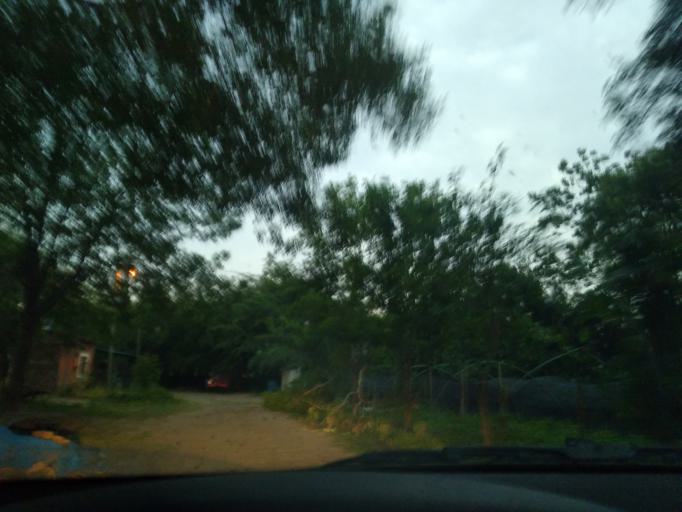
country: AR
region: Chaco
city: Puerto Tirol
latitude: -27.3758
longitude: -59.0842
